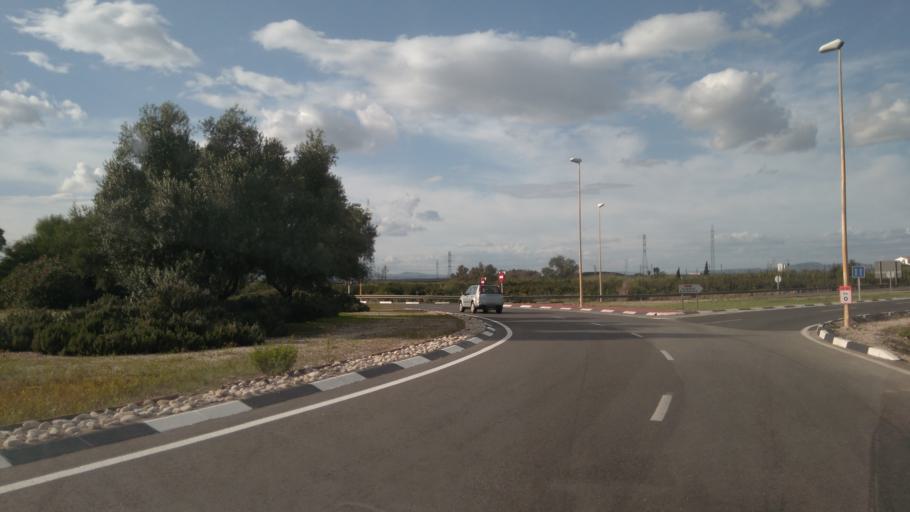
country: ES
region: Valencia
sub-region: Provincia de Valencia
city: Alzira
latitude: 39.1636
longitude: -0.4448
